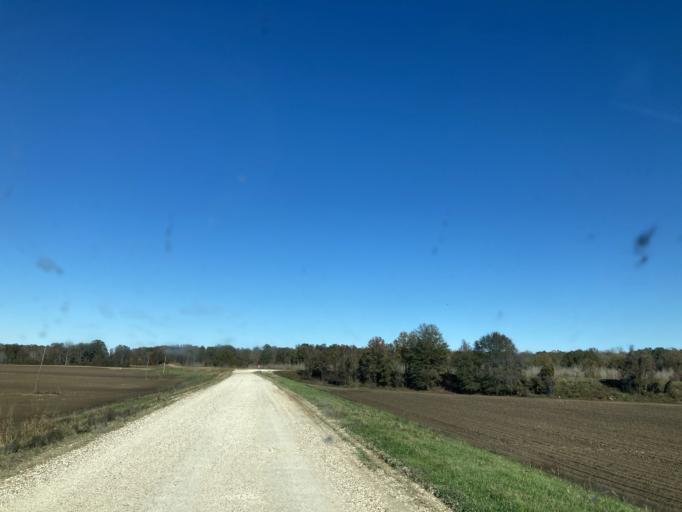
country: US
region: Mississippi
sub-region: Yazoo County
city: Yazoo City
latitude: 32.7758
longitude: -90.6398
